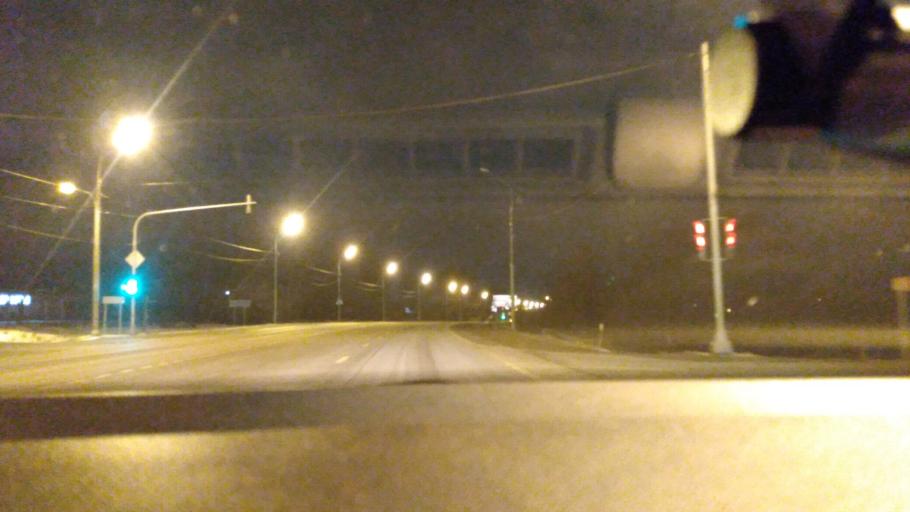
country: RU
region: Moskovskaya
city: Bronnitsy
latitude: 55.4024
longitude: 38.3054
